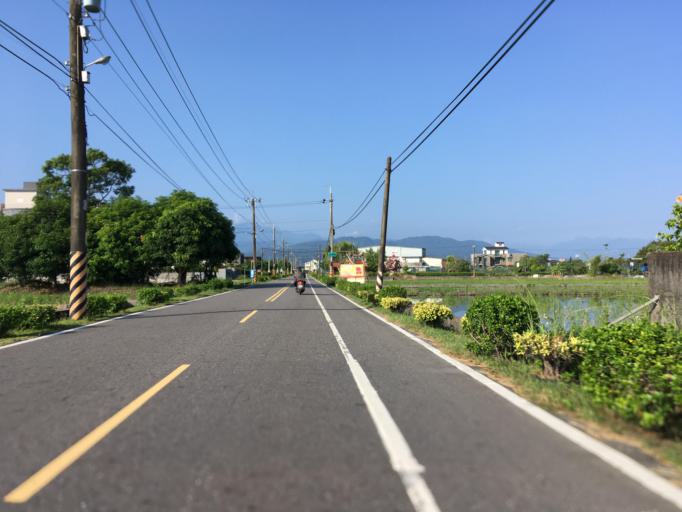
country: TW
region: Taiwan
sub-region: Yilan
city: Yilan
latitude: 24.6834
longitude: 121.7403
